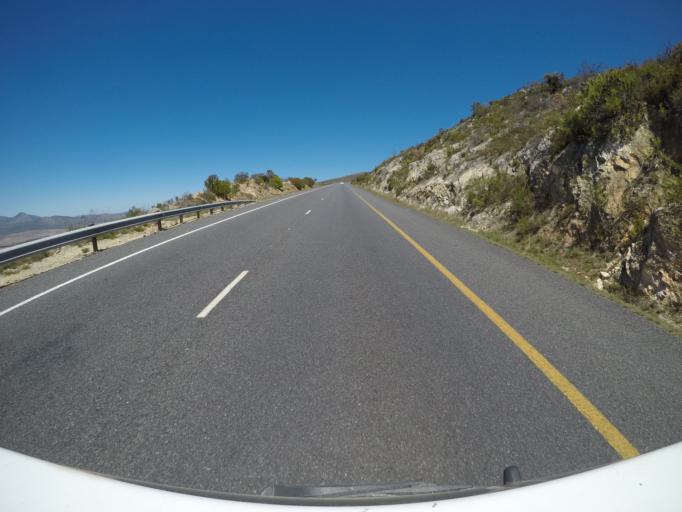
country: ZA
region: Western Cape
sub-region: Overberg District Municipality
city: Grabouw
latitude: -34.2195
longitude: 19.1851
